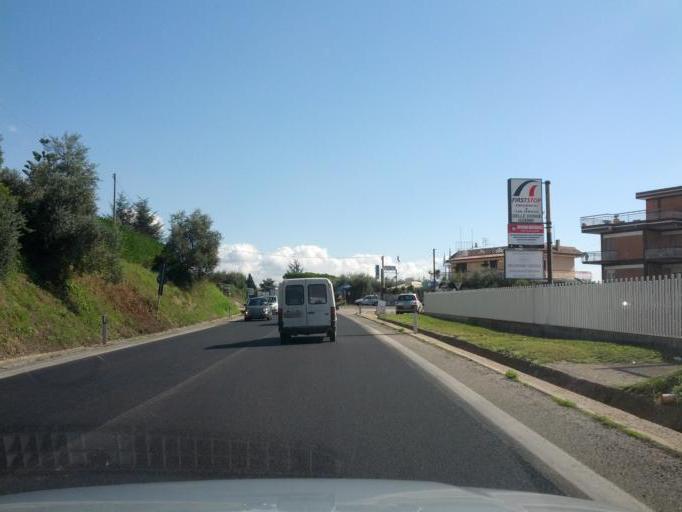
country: IT
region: Latium
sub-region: Provincia di Latina
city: Formia
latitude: 41.2659
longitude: 13.6499
